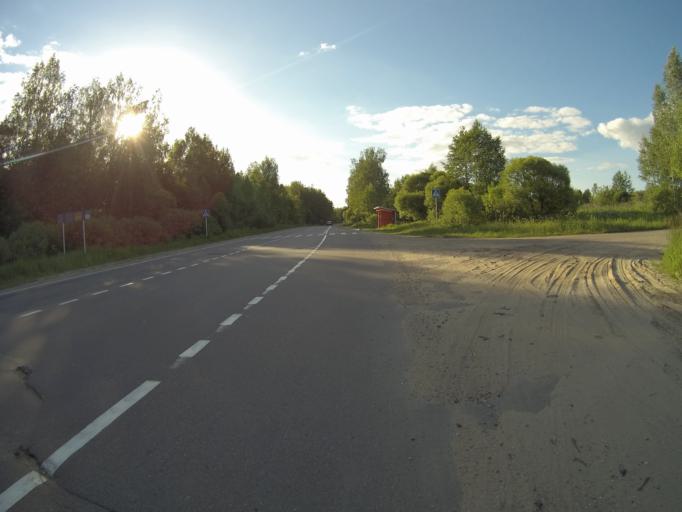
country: RU
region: Vladimir
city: Anopino
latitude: 55.8528
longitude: 40.6446
